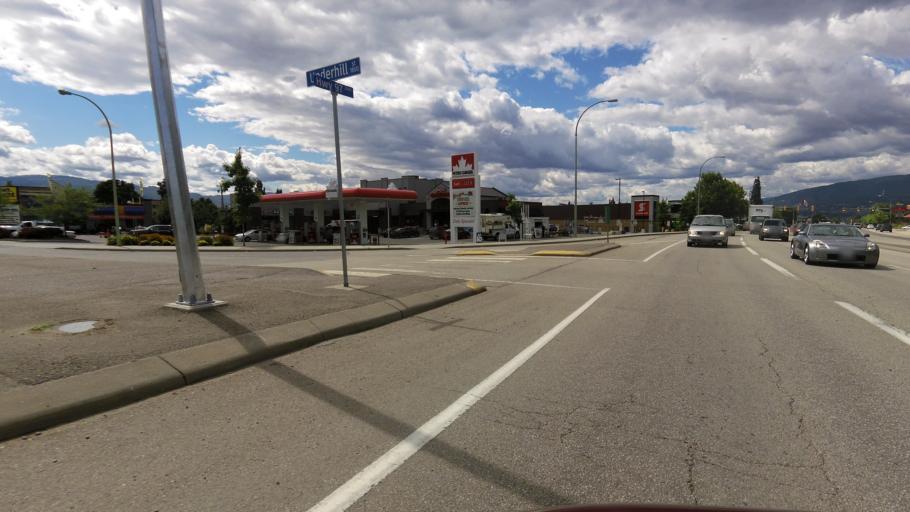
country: CA
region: British Columbia
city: Kelowna
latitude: 49.8819
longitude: -119.4349
